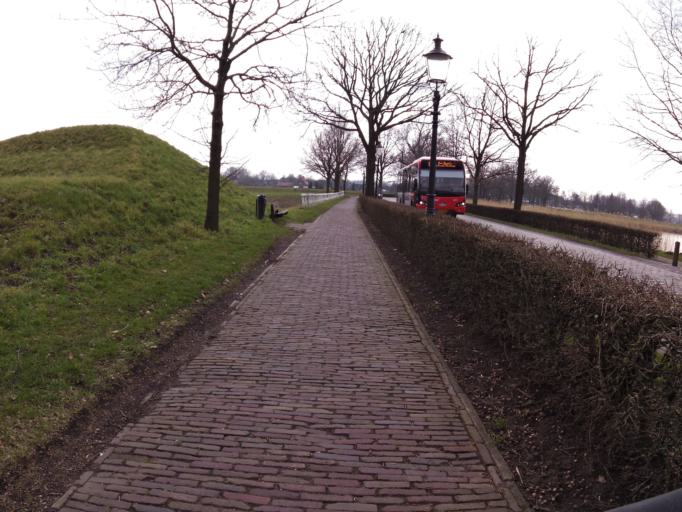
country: NL
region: North Brabant
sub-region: Gemeente Heusden
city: Heusden
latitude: 51.7306
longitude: 5.1386
